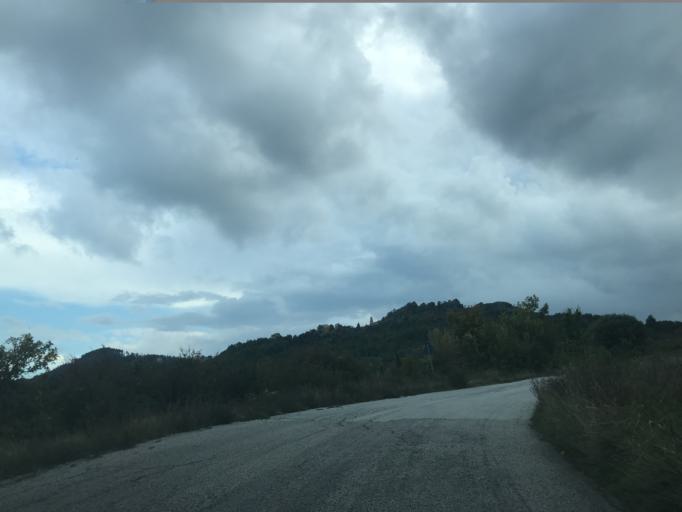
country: IT
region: Molise
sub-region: Provincia di Campobasso
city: Duronia
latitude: 41.6697
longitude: 14.4610
